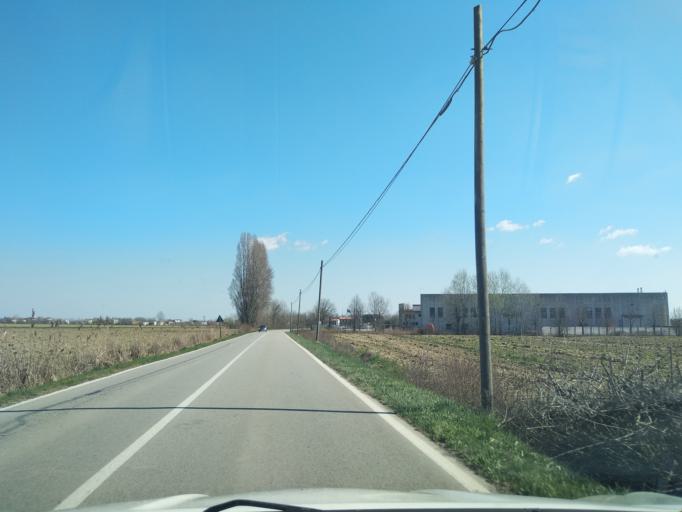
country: IT
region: Veneto
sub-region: Provincia di Padova
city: Taggi
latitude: 45.4644
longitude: 11.8041
